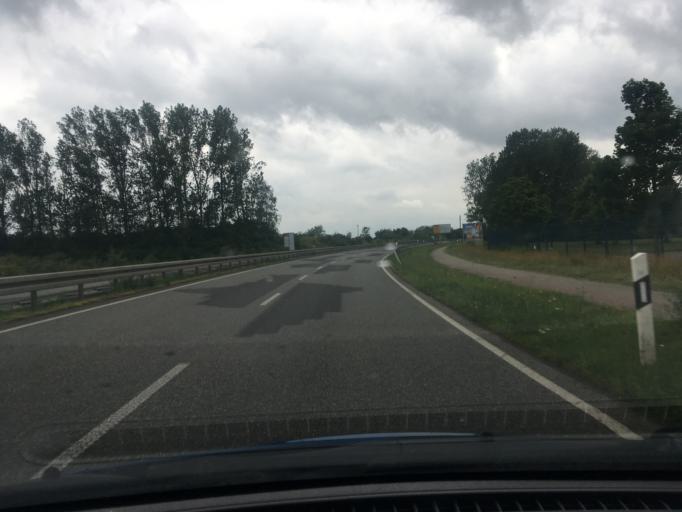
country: DE
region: Mecklenburg-Vorpommern
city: Klein Rogahn
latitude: 53.5703
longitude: 11.3858
